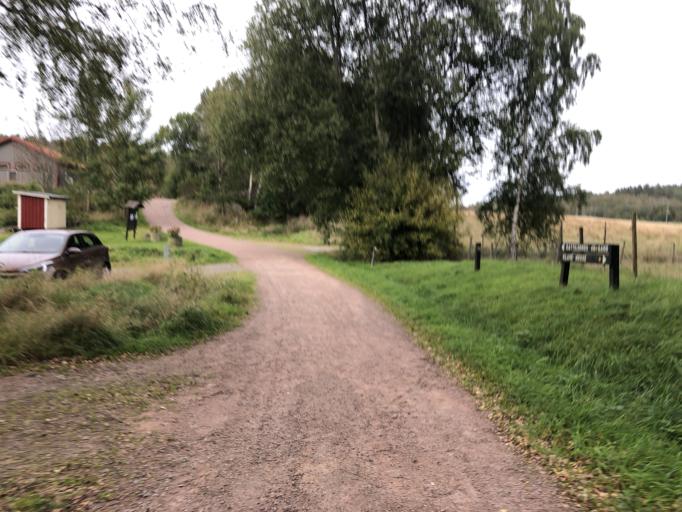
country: SE
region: Vaestra Goetaland
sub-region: Goteborg
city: Majorna
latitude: 57.7483
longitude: 11.9005
